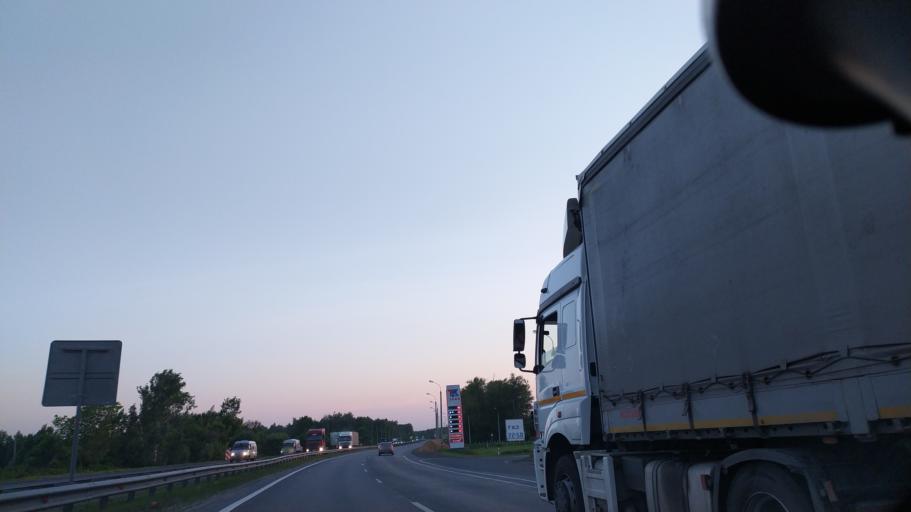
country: RU
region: Chuvashia
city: Ishley
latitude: 56.1001
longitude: 47.0308
